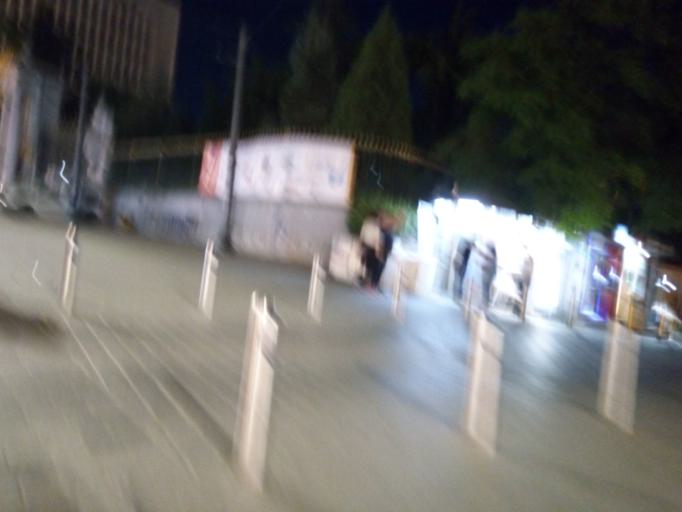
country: TR
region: Istanbul
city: Eminoenue
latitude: 41.0335
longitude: 28.9772
